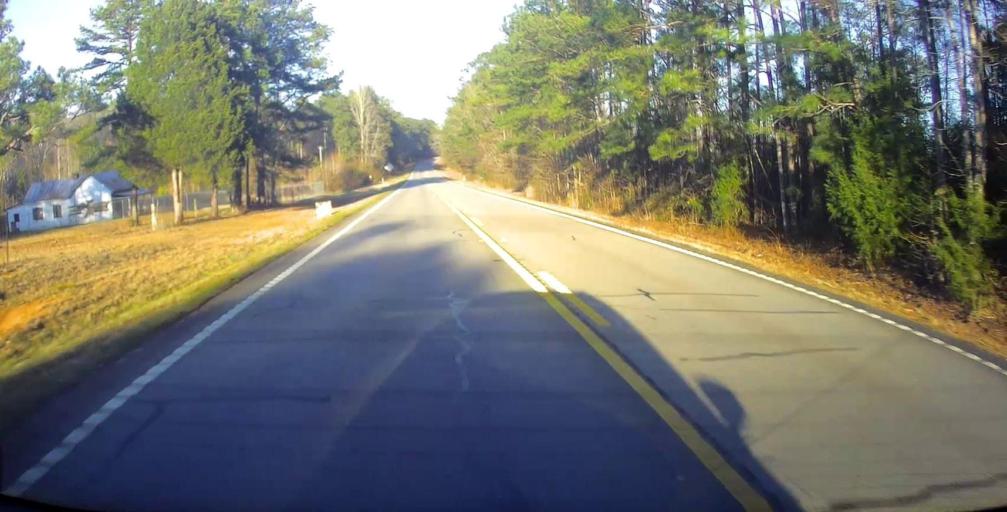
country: US
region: Georgia
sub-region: Harris County
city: Pine Mountain
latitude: 32.8474
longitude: -84.8928
